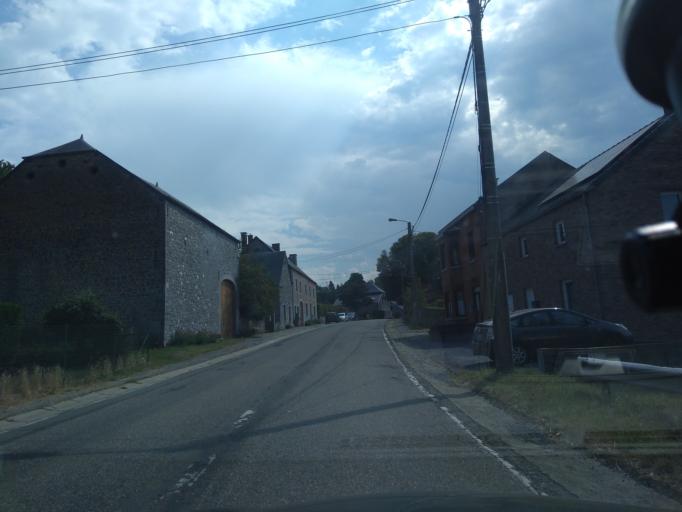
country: BE
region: Wallonia
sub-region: Province de Namur
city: Dinant
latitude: 50.2072
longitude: 4.8971
